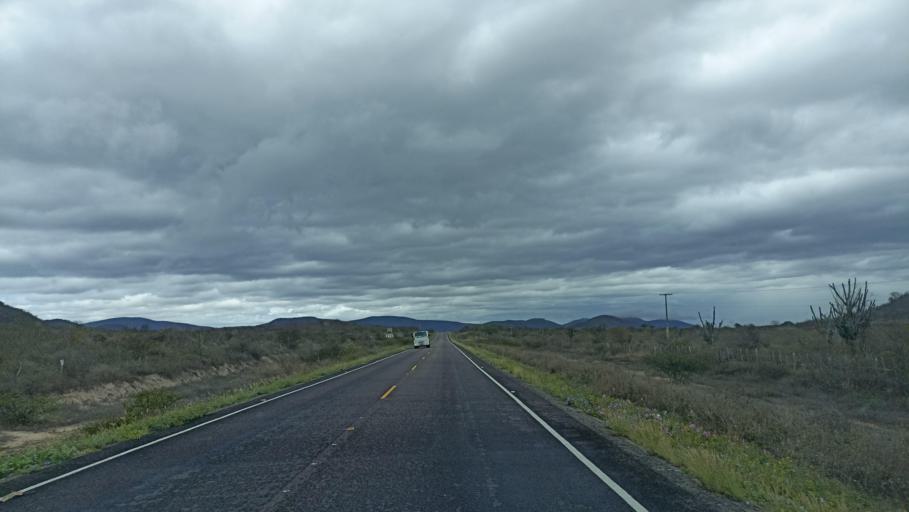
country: BR
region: Bahia
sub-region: Iacu
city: Iacu
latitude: -12.9065
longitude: -40.4055
